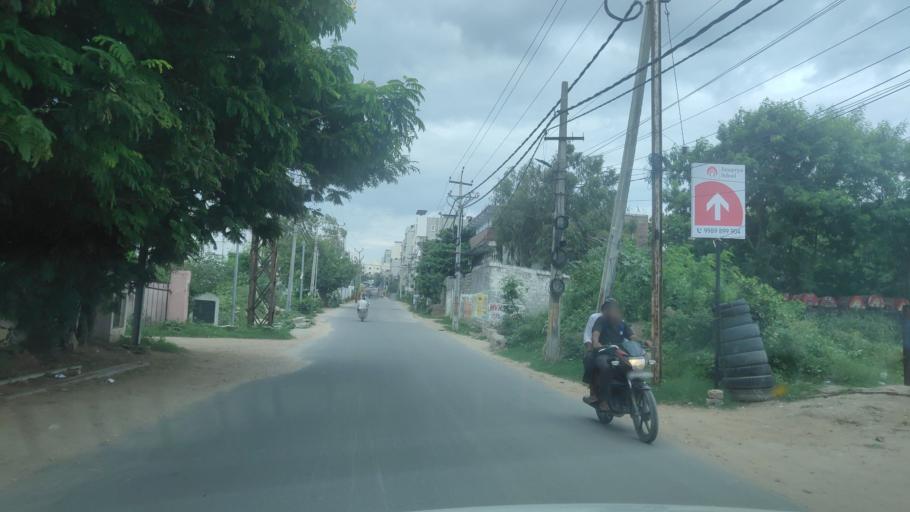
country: IN
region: Telangana
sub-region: Medak
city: Serilingampalle
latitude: 17.4966
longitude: 78.3485
